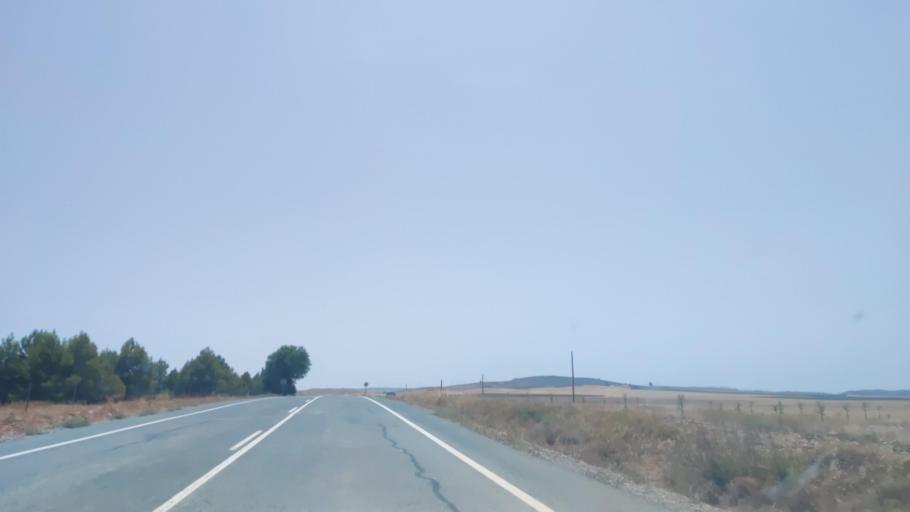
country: ES
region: Castille-La Mancha
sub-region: Provincia de Albacete
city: Pozo-Canada
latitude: 38.8474
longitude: -1.7659
